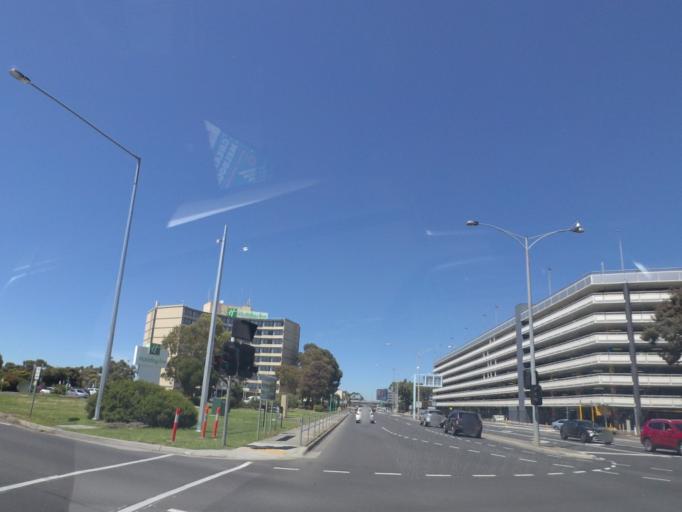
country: AU
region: Victoria
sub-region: Hume
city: Attwood
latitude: -37.6707
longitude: 144.8532
